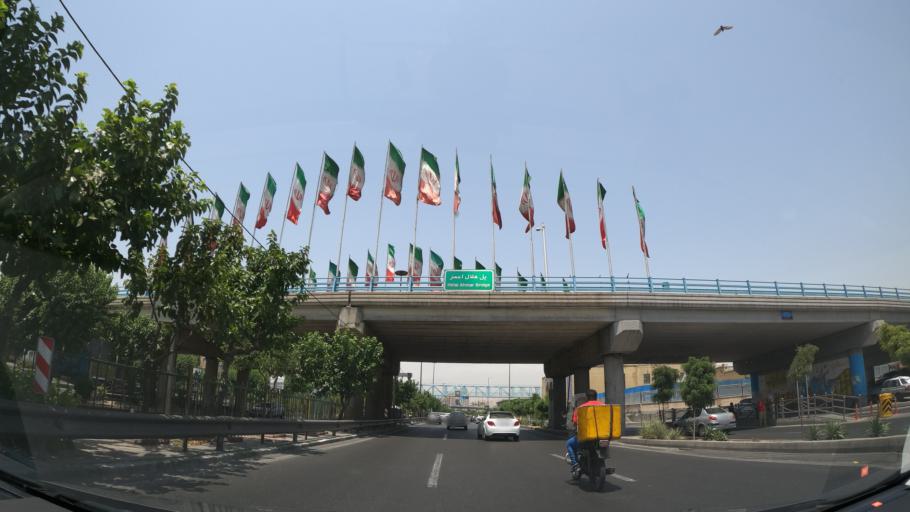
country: IR
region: Tehran
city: Tehran
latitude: 35.6677
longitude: 51.3818
